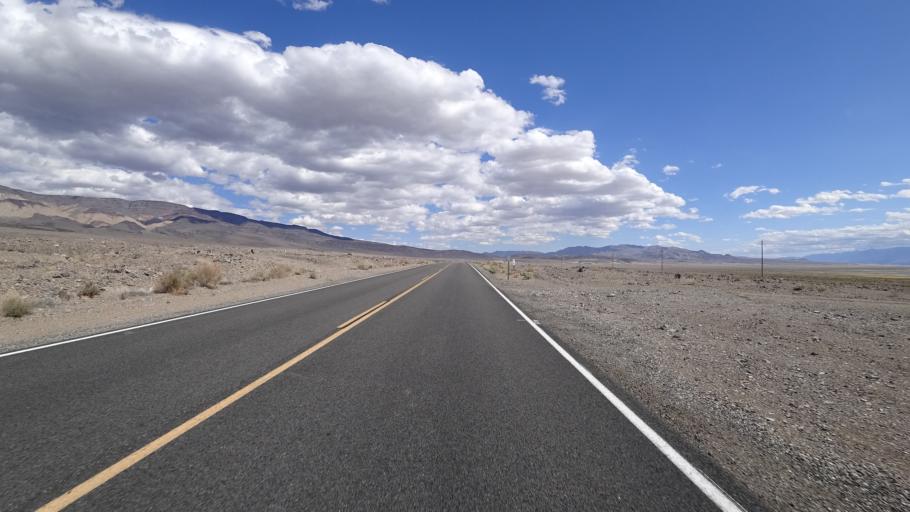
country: US
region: California
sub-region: Inyo County
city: Lone Pine
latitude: 36.4520
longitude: -117.8400
